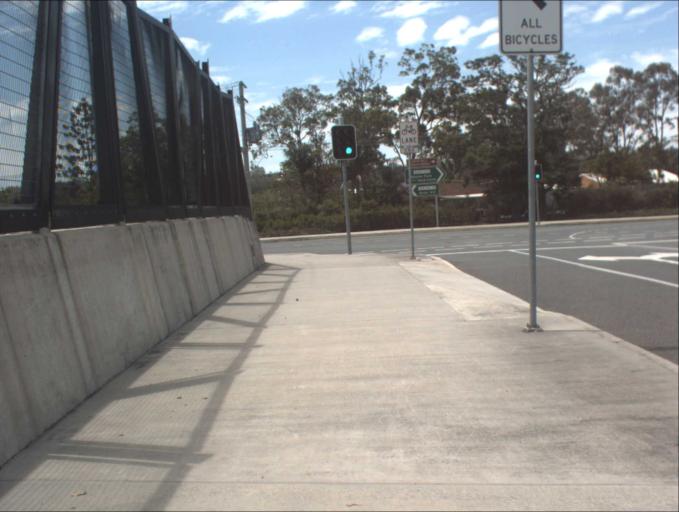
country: AU
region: Queensland
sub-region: Logan
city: Slacks Creek
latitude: -27.6436
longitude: 153.1457
